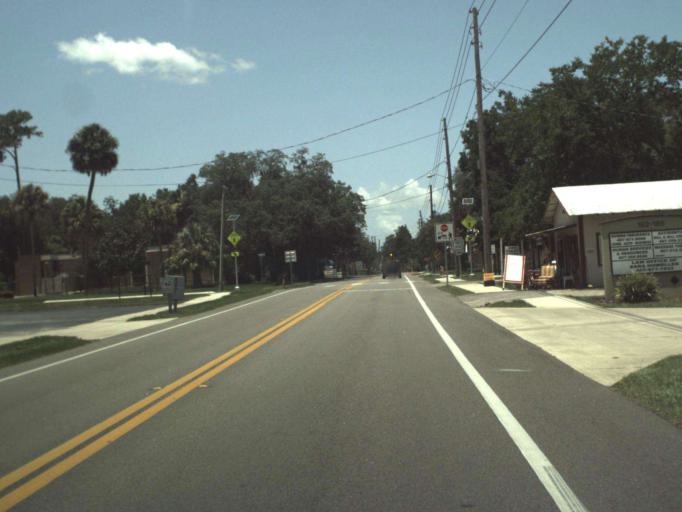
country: US
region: Florida
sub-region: Seminole County
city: Oviedo
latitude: 28.6675
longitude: -81.2084
